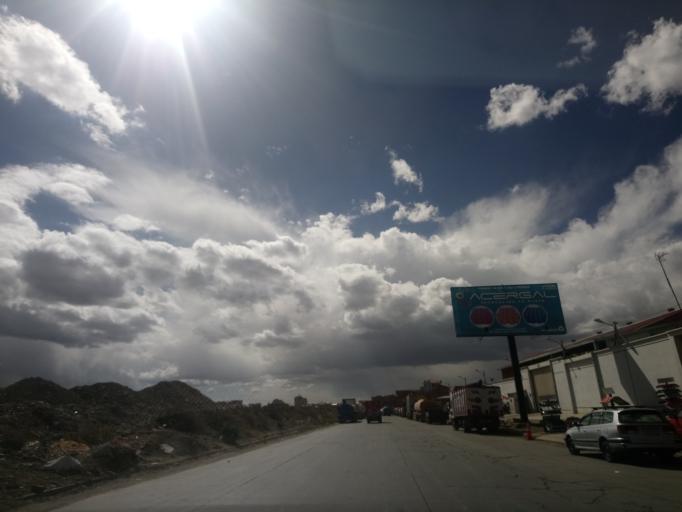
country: BO
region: La Paz
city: La Paz
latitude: -16.5529
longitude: -68.1830
